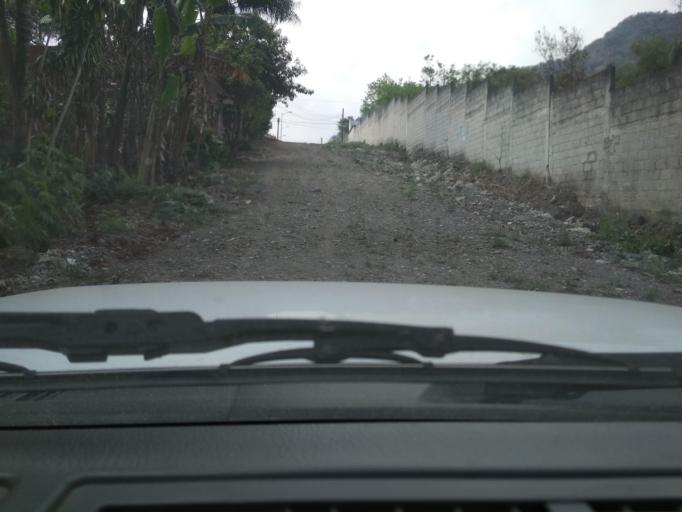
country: MX
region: Veracruz
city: Orizaba
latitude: 18.8684
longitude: -97.0944
